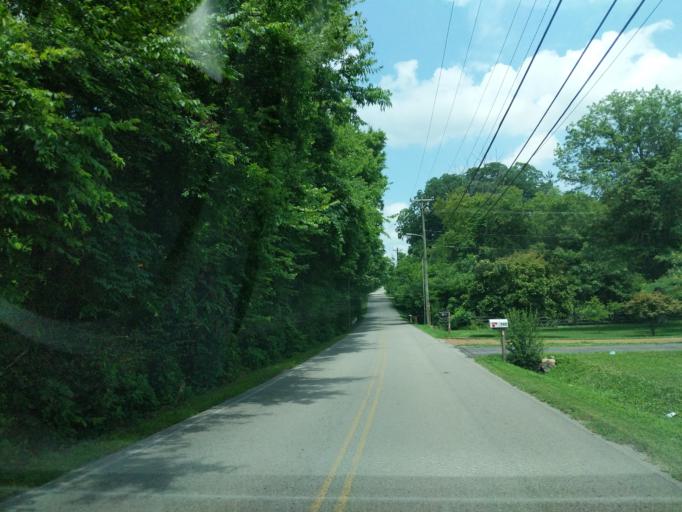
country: US
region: Tennessee
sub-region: Davidson County
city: Goodlettsville
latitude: 36.3041
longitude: -86.7246
